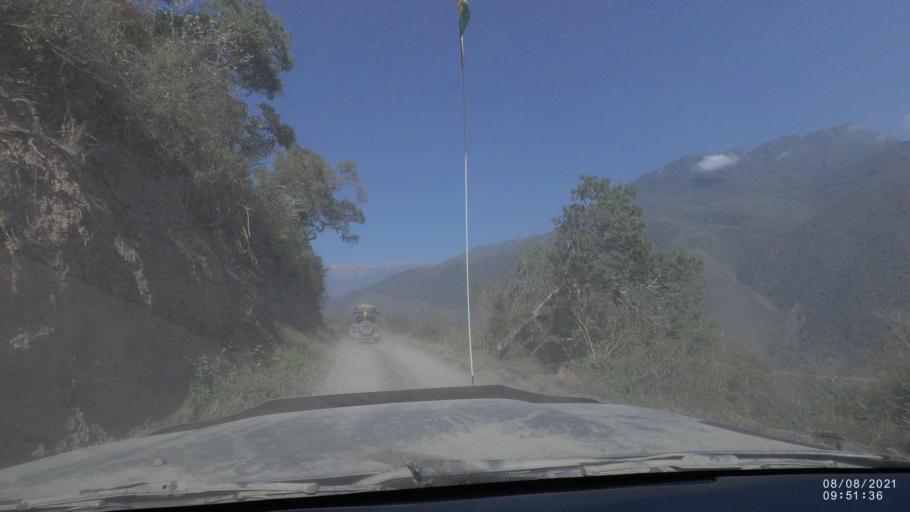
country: BO
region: La Paz
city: Quime
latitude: -16.6232
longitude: -66.7288
